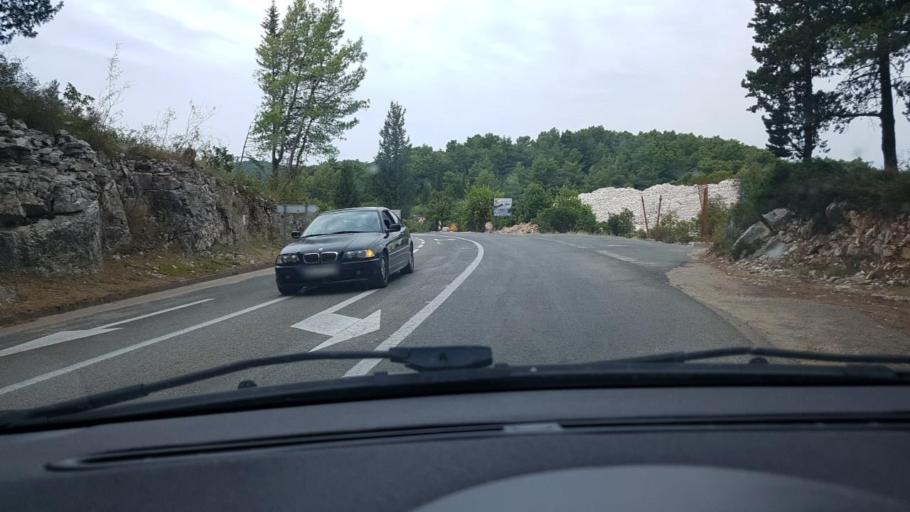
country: HR
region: Dubrovacko-Neretvanska
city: Korcula
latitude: 42.9546
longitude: 17.1286
